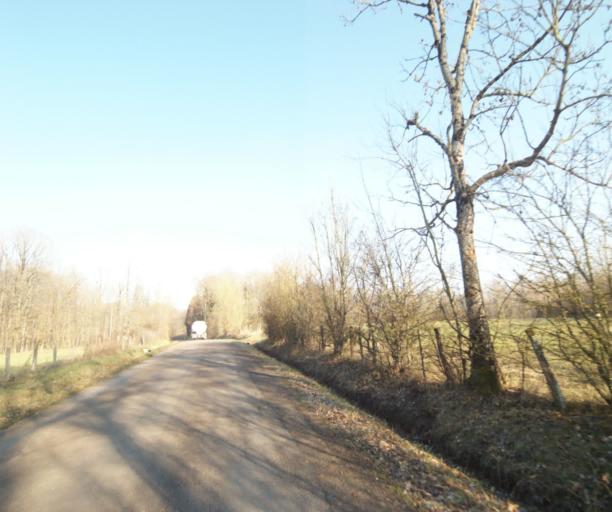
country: FR
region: Champagne-Ardenne
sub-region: Departement de la Haute-Marne
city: Wassy
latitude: 48.5083
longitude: 4.9634
